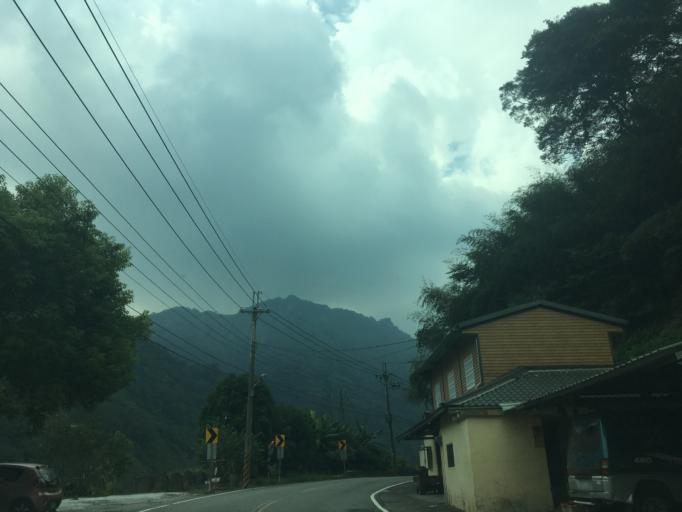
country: TW
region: Taiwan
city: Fengyuan
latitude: 24.3282
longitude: 120.9196
